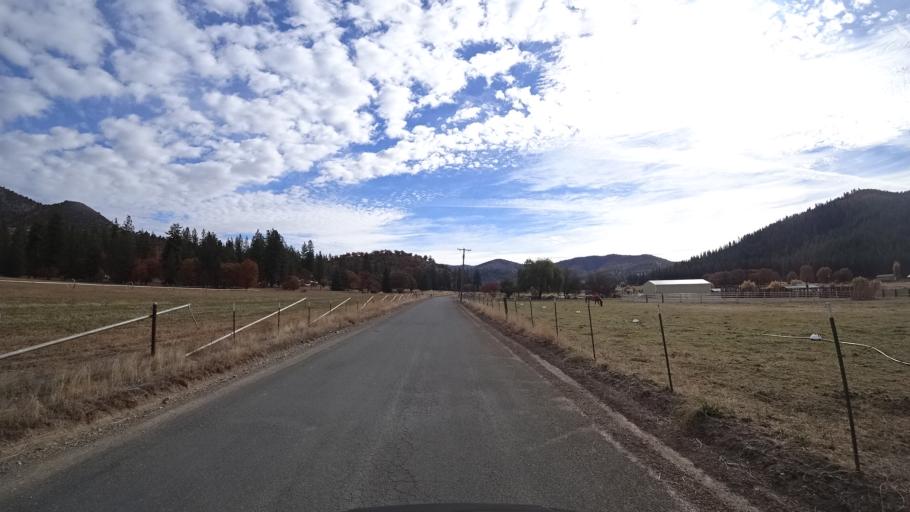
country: US
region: California
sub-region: Siskiyou County
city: Yreka
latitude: 41.6260
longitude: -122.8003
